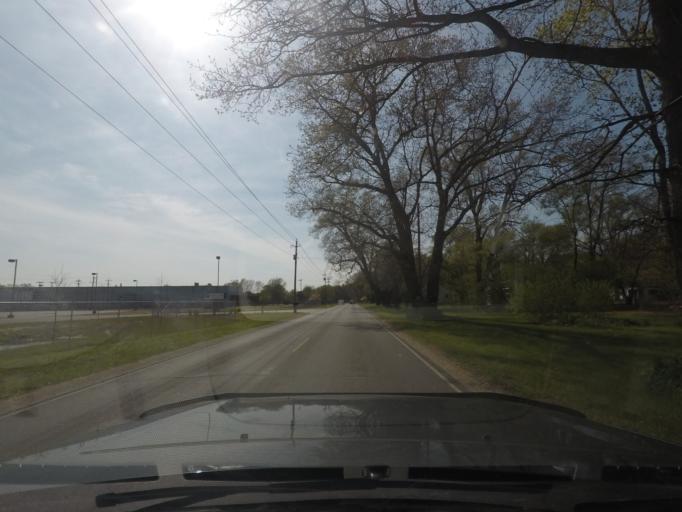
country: US
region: Indiana
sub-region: Elkhart County
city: Elkhart
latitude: 41.7046
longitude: -86.0092
